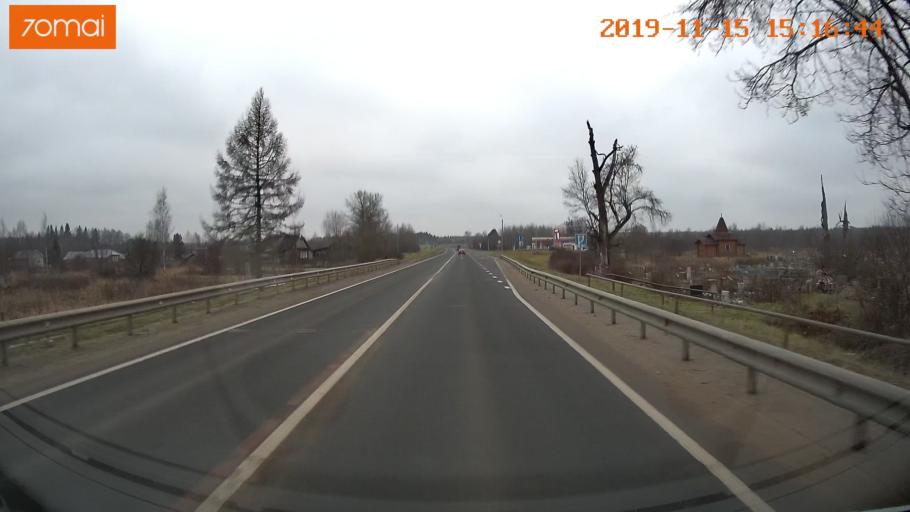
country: RU
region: Jaroslavl
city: Danilov
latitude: 58.2700
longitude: 40.1880
